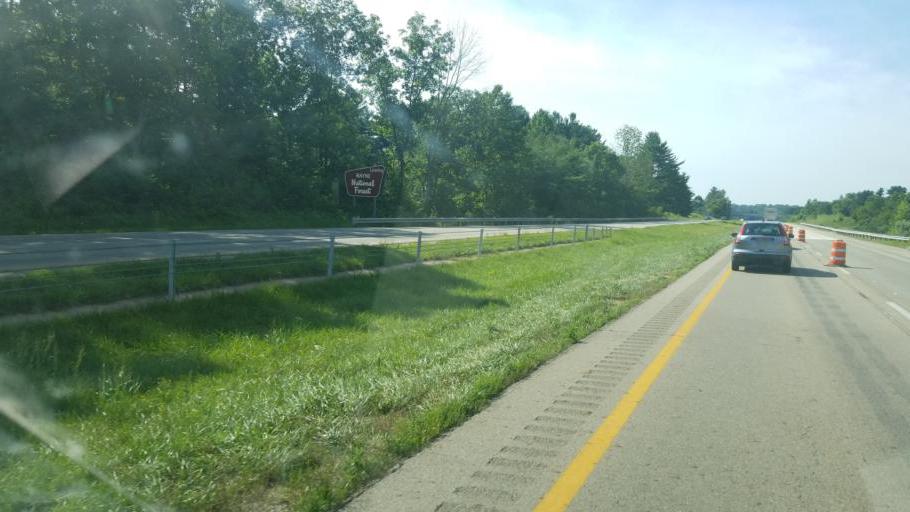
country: US
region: Ohio
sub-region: Athens County
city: Nelsonville
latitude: 39.4813
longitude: -82.3173
